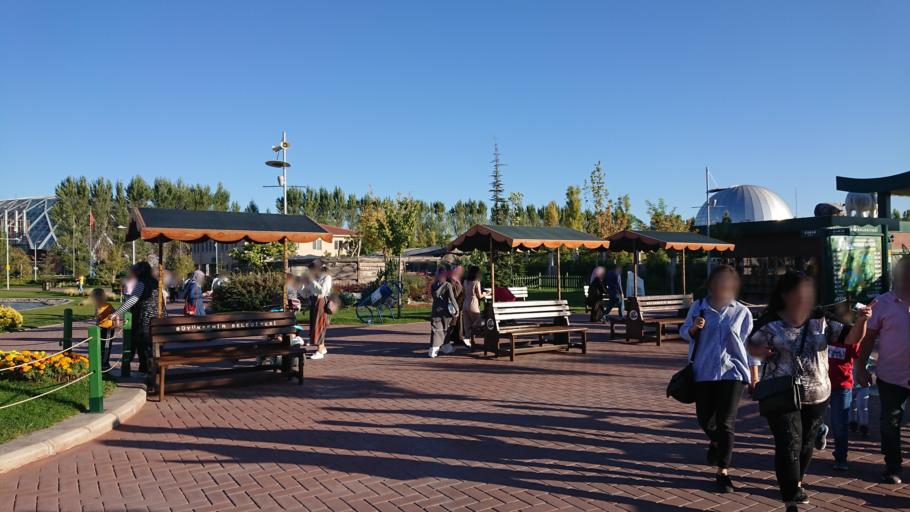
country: TR
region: Eskisehir
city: Eskisehir
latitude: 39.7674
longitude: 30.4735
